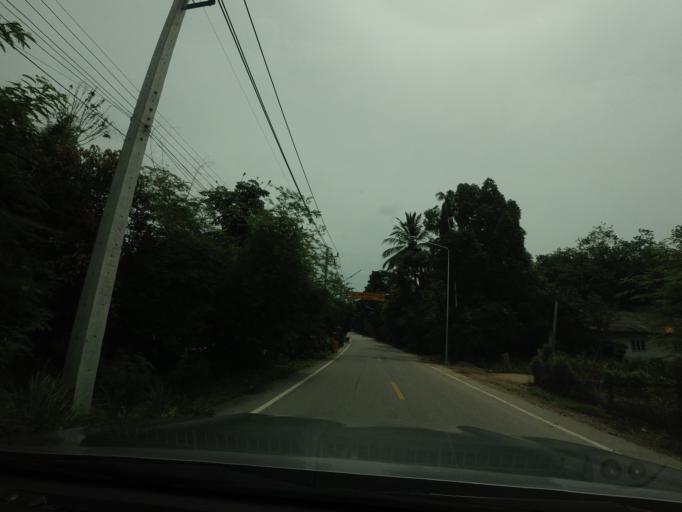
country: TH
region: Pattani
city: Kapho
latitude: 6.5731
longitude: 101.5348
